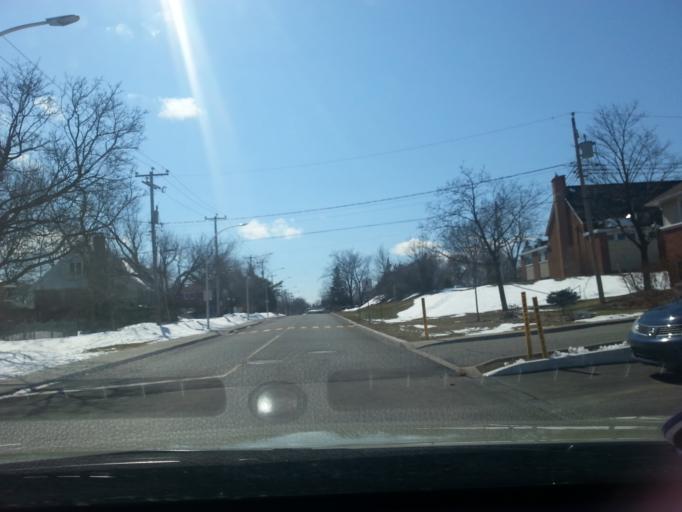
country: CA
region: Quebec
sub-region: Montreal
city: Pointe-Claire
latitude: 45.4580
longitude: -73.8144
